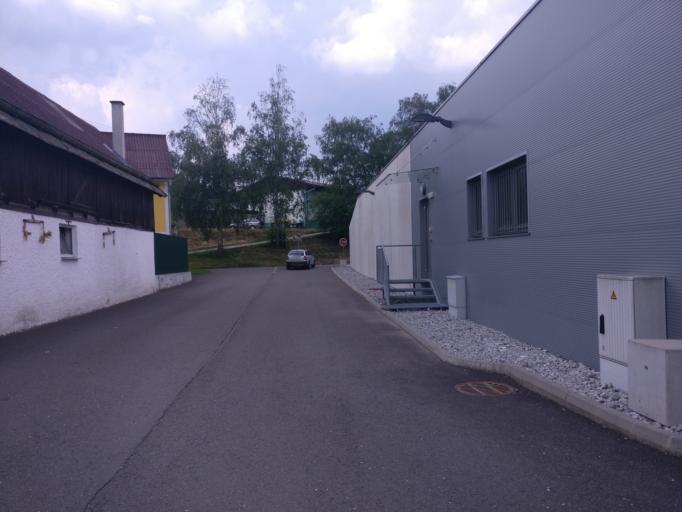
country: AT
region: Styria
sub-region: Politischer Bezirk Bruck-Muerzzuschlag
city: Krieglach
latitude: 47.5474
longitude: 15.5620
